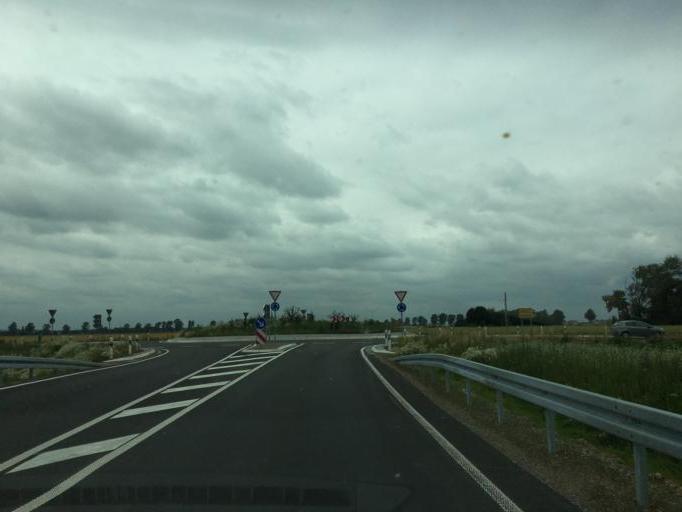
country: DE
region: North Rhine-Westphalia
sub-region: Regierungsbezirk Koln
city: Merzenich
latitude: 50.7905
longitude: 6.5697
